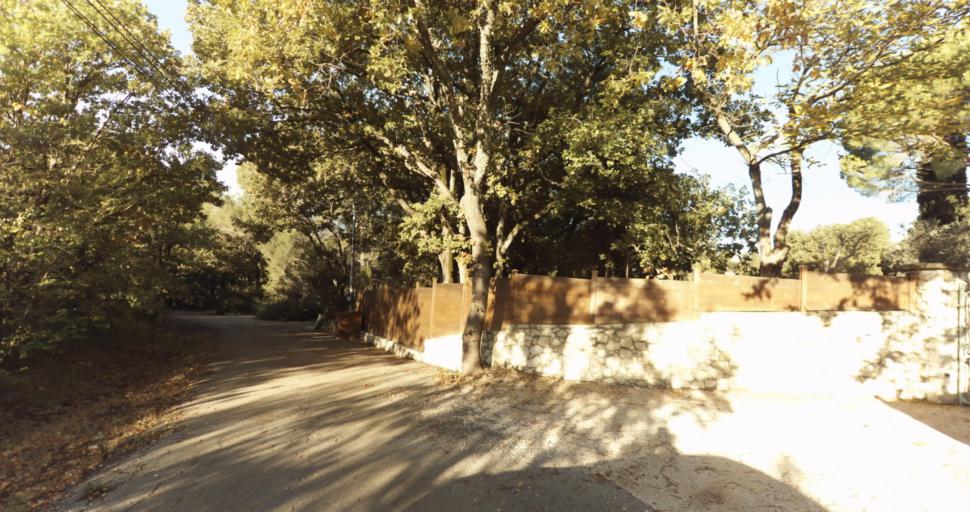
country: FR
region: Provence-Alpes-Cote d'Azur
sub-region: Departement des Bouches-du-Rhone
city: Venelles
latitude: 43.6023
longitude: 5.4712
